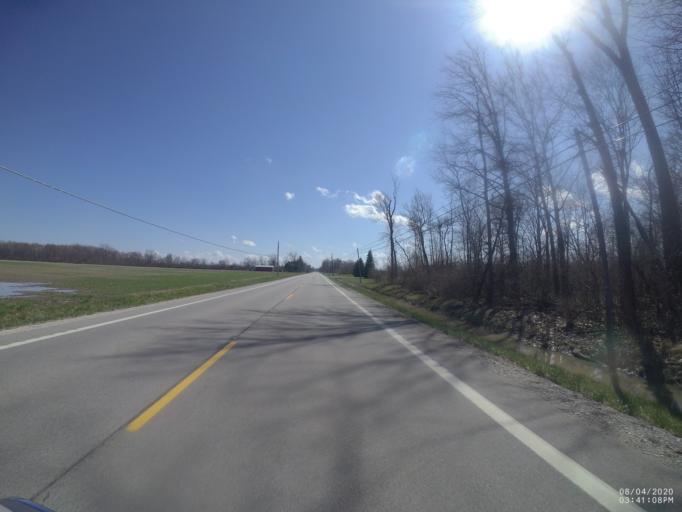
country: US
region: Ohio
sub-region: Sandusky County
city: Stony Prairie
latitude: 41.2653
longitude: -83.2353
